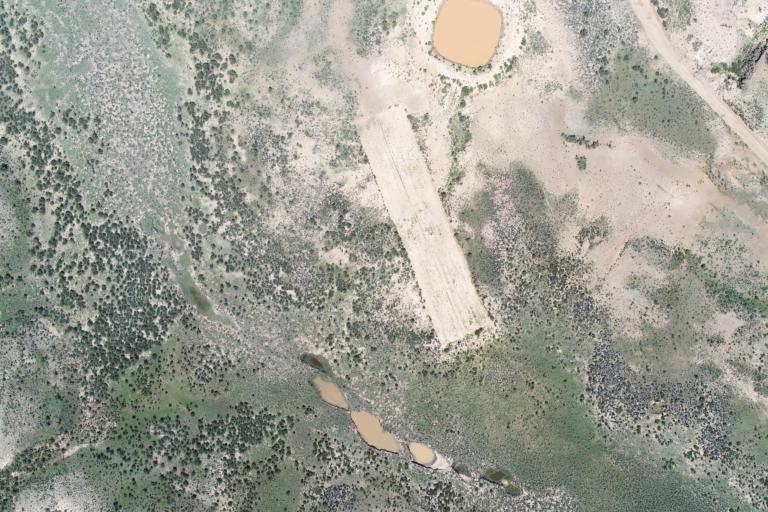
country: BO
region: La Paz
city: Curahuara de Carangas
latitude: -17.2946
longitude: -68.5154
